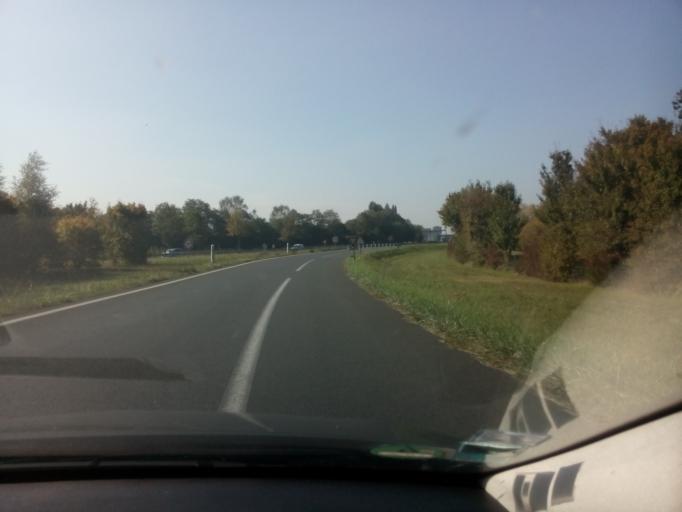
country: FR
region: Pays de la Loire
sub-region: Departement de Maine-et-Loire
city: Pellouailles-les-Vignes
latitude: 47.5196
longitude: -0.4285
